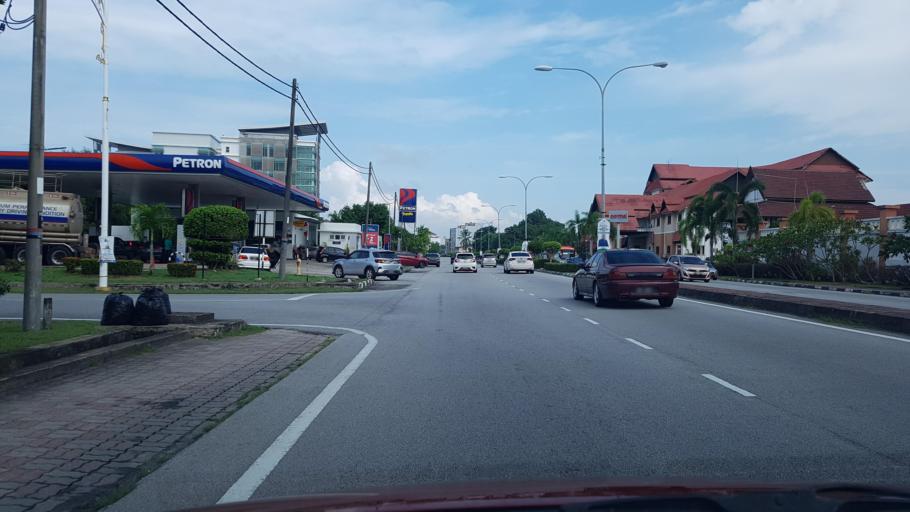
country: MY
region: Terengganu
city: Kuala Terengganu
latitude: 5.3161
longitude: 103.1544
